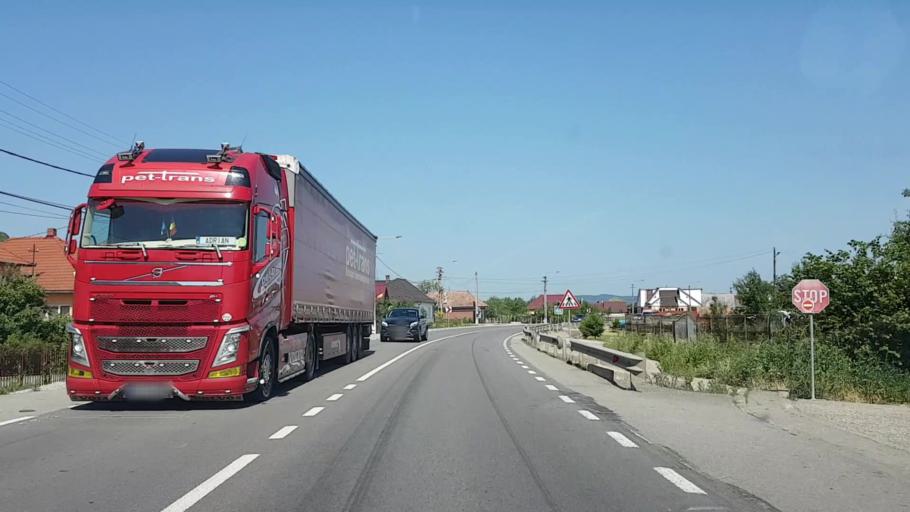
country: RO
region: Bistrita-Nasaud
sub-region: Comuna Petru Rares
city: Reteag
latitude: 47.1970
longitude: 24.0205
